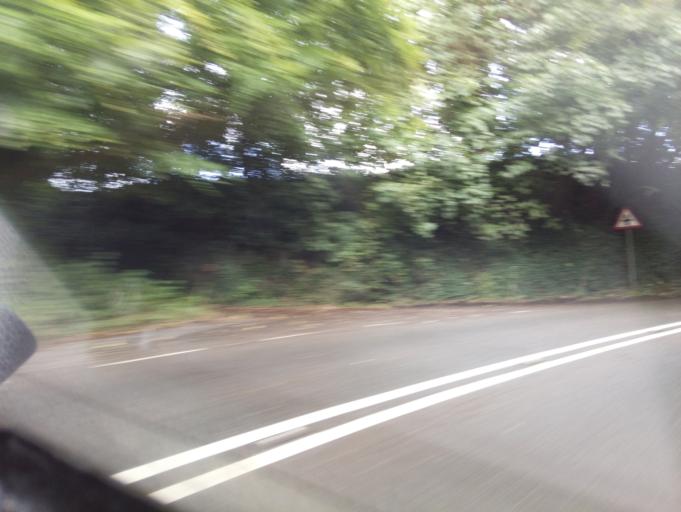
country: GB
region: England
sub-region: Devon
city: Modbury
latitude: 50.3502
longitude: -3.9217
